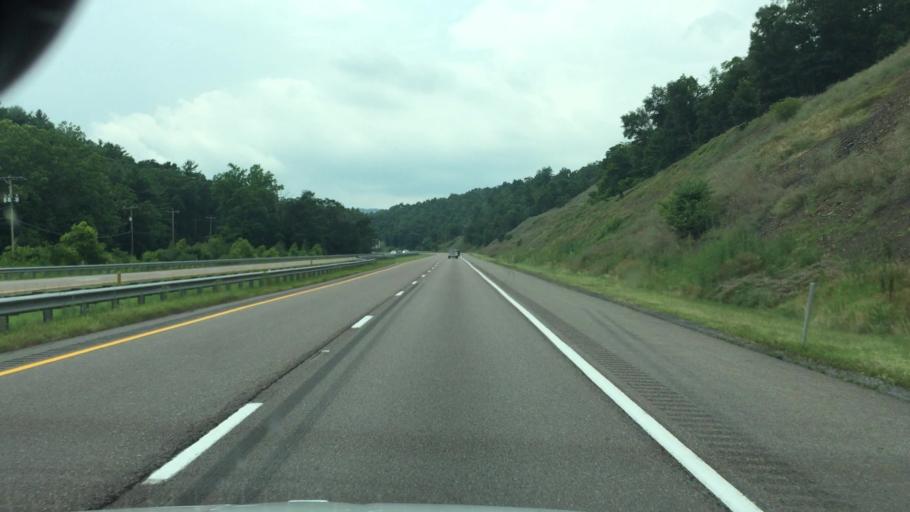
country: US
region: West Virginia
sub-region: Morgan County
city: Berkeley Springs
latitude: 39.6794
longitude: -78.4778
